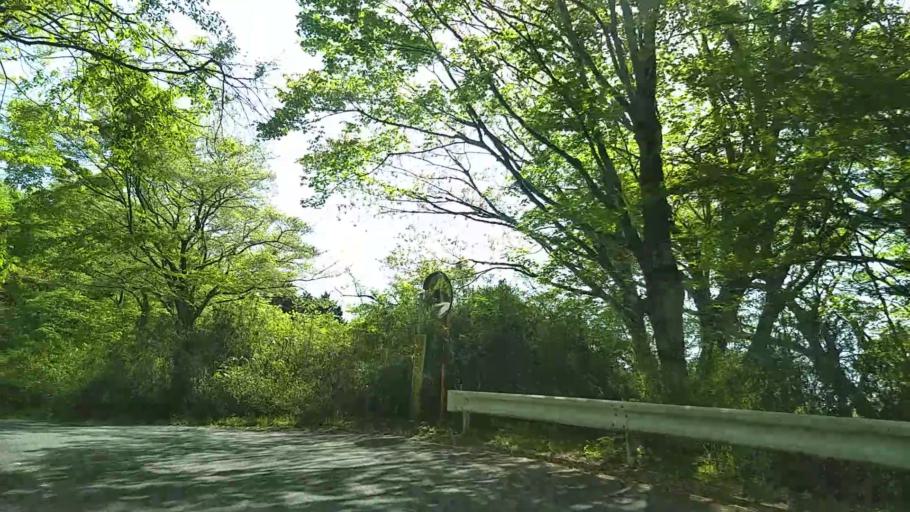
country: JP
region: Shizuoka
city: Gotemba
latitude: 35.2656
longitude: 138.9667
